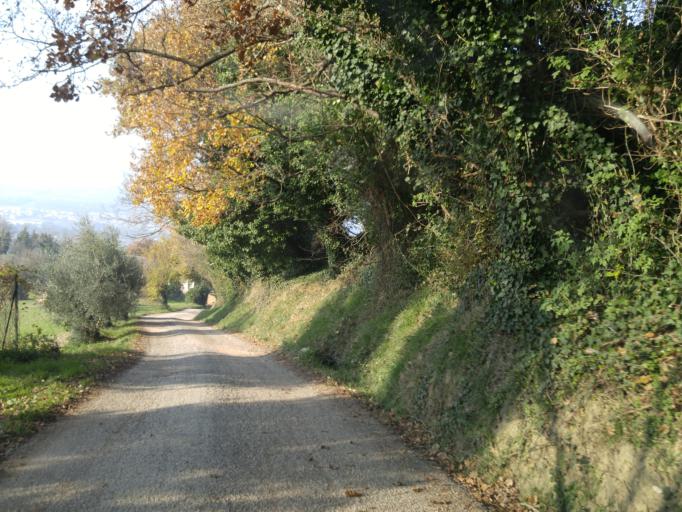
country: IT
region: The Marches
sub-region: Provincia di Pesaro e Urbino
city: Villanova
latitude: 43.7251
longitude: 12.9249
